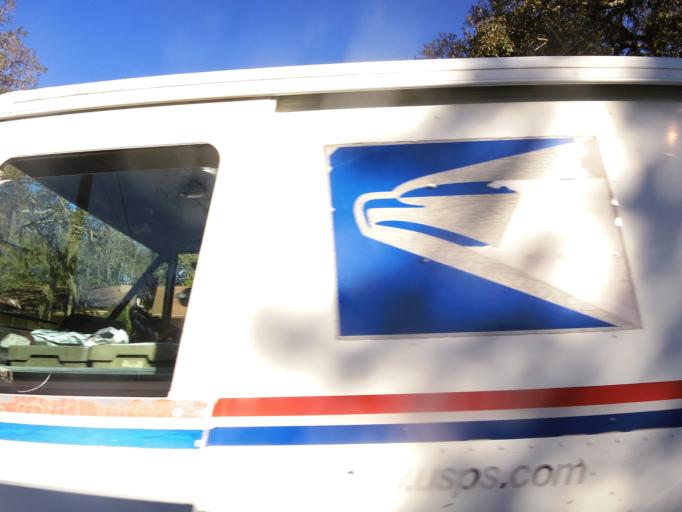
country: US
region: Florida
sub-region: Duval County
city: Jacksonville
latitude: 30.3999
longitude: -81.6768
